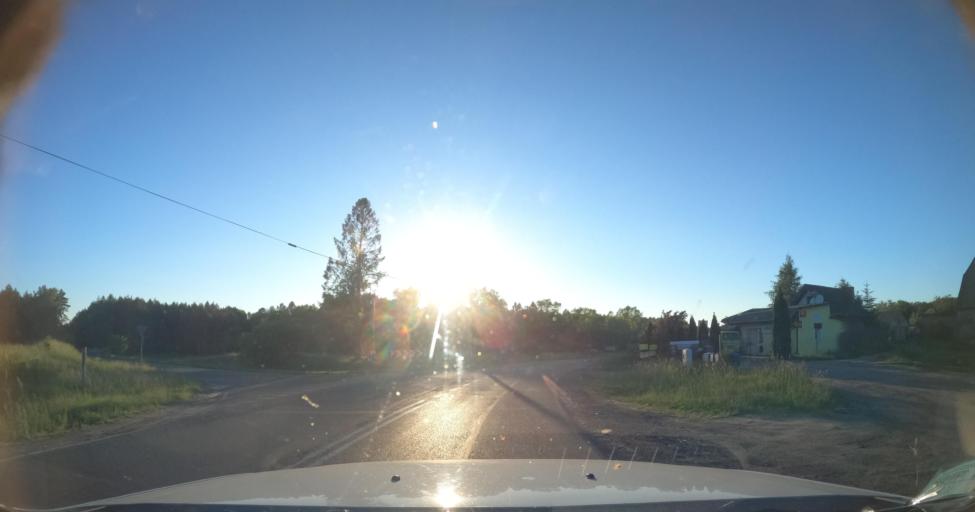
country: PL
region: Pomeranian Voivodeship
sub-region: Powiat bytowski
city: Czarna Dabrowka
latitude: 54.3667
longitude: 17.5054
